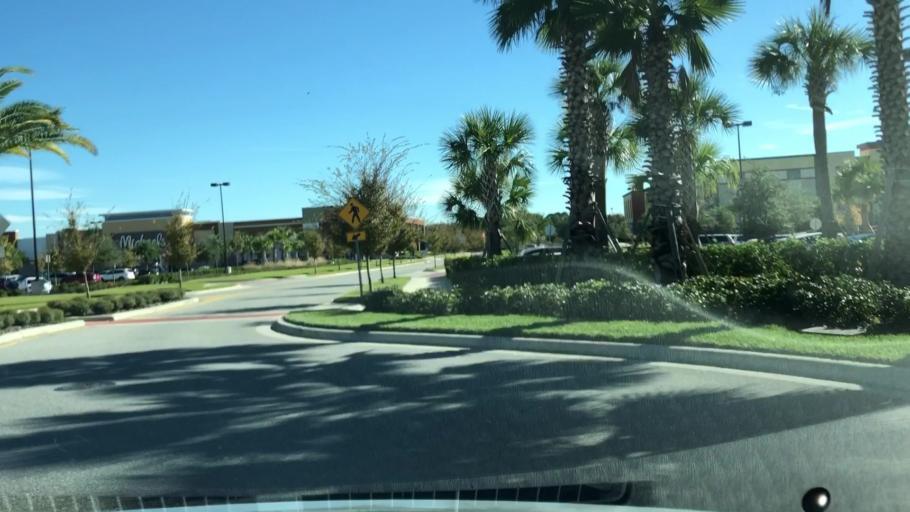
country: US
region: Florida
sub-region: Orange County
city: Conway
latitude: 28.4653
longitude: -81.3064
